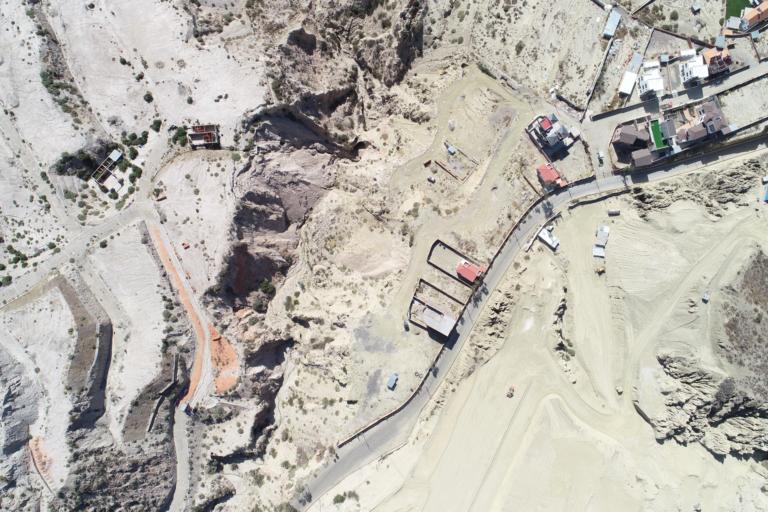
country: BO
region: La Paz
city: La Paz
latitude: -16.5575
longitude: -68.1070
